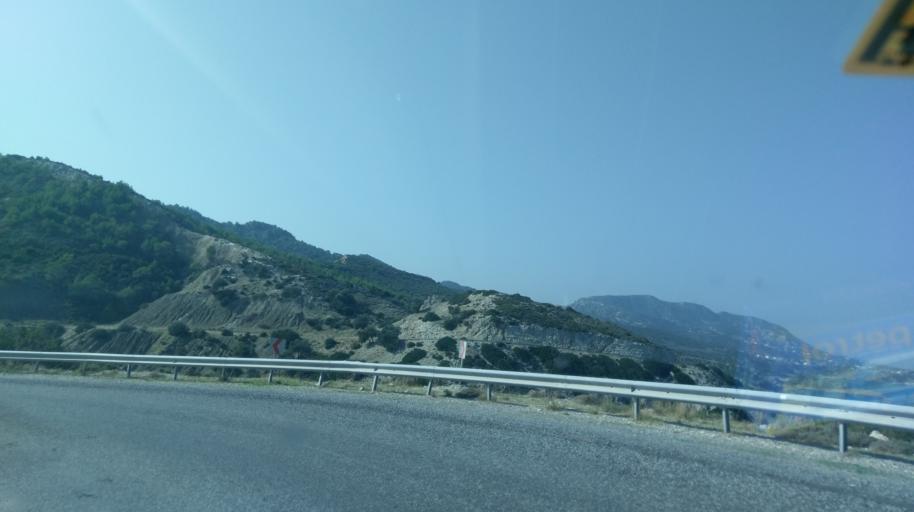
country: CY
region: Keryneia
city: Lapithos
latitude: 35.3541
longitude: 33.0744
